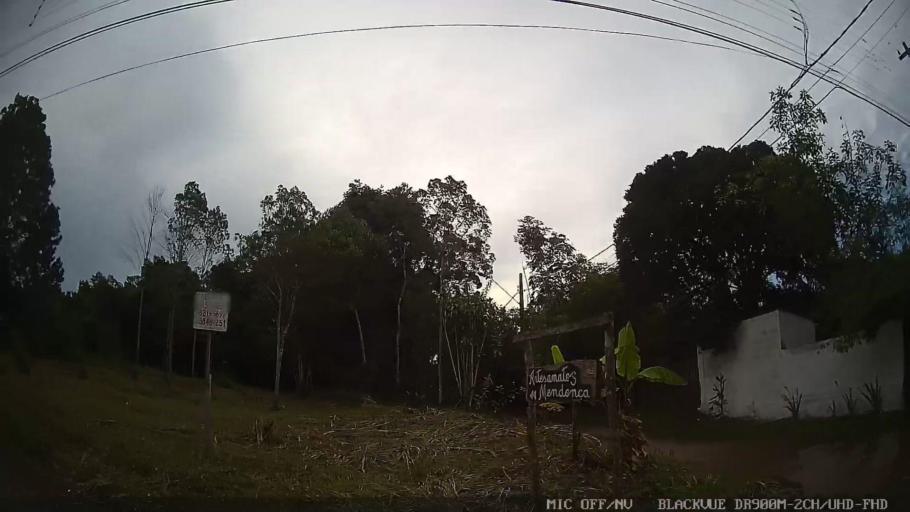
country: BR
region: Sao Paulo
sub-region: Iguape
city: Iguape
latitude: -24.6751
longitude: -47.4522
